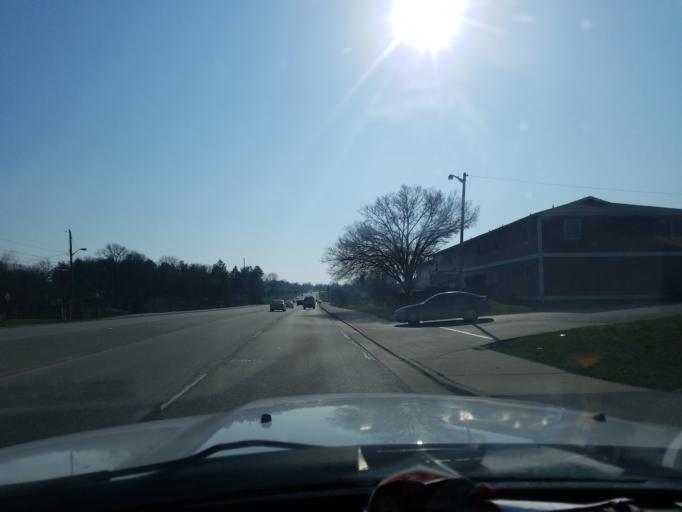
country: US
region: Indiana
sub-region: Monroe County
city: Bloomington
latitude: 39.1863
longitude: -86.5322
